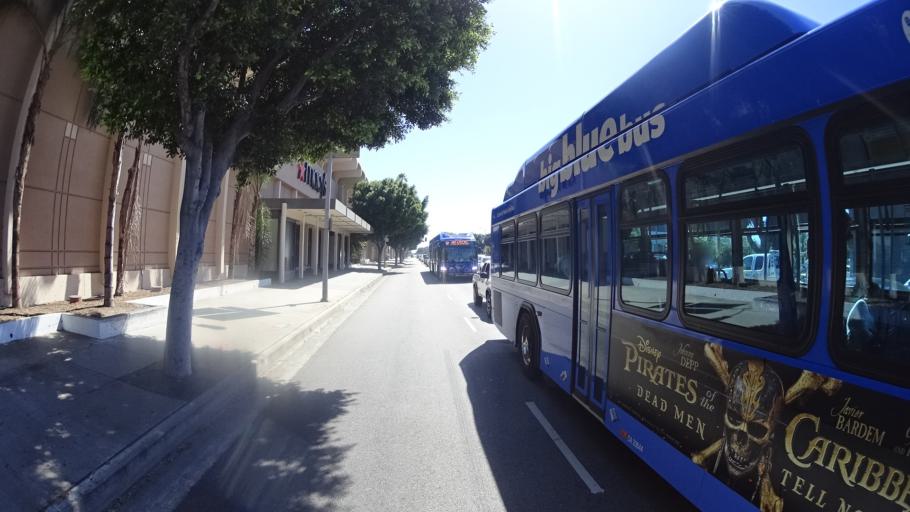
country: US
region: California
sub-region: Los Angeles County
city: Westwood, Los Angeles
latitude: 34.0416
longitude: -118.4252
